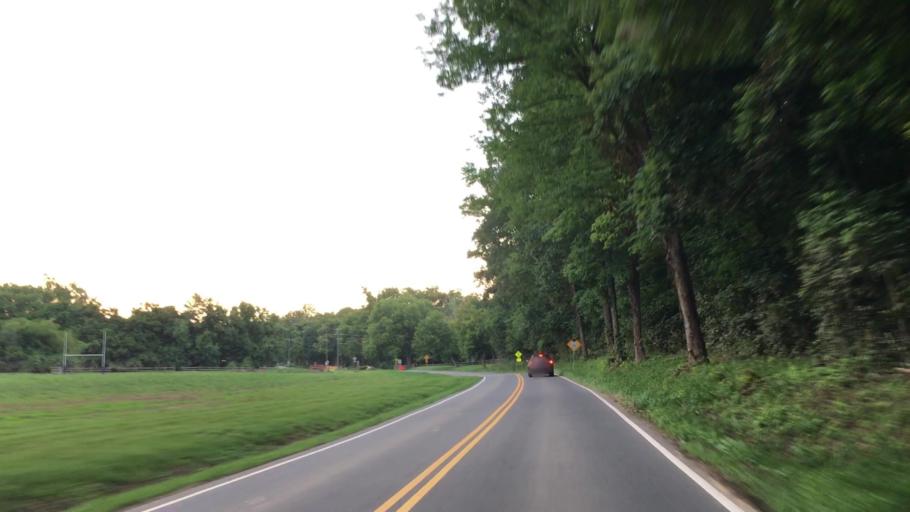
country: US
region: Virginia
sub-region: Stafford County
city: Falmouth
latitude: 38.3194
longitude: -77.4645
